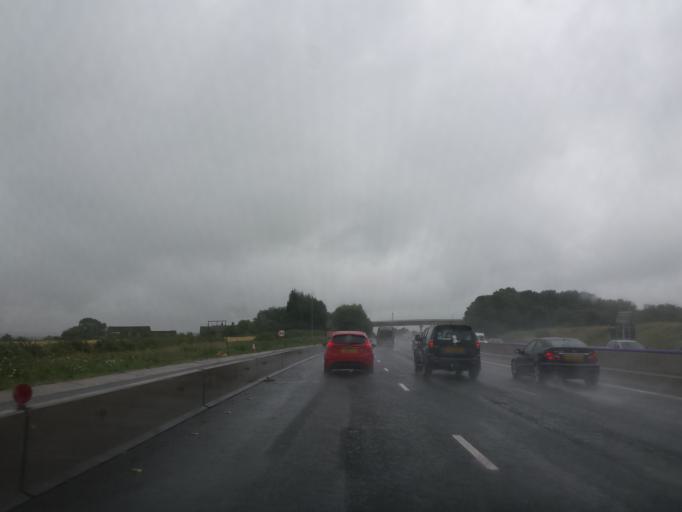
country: GB
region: England
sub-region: Derbyshire
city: Blackwell
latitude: 53.1324
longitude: -1.3291
